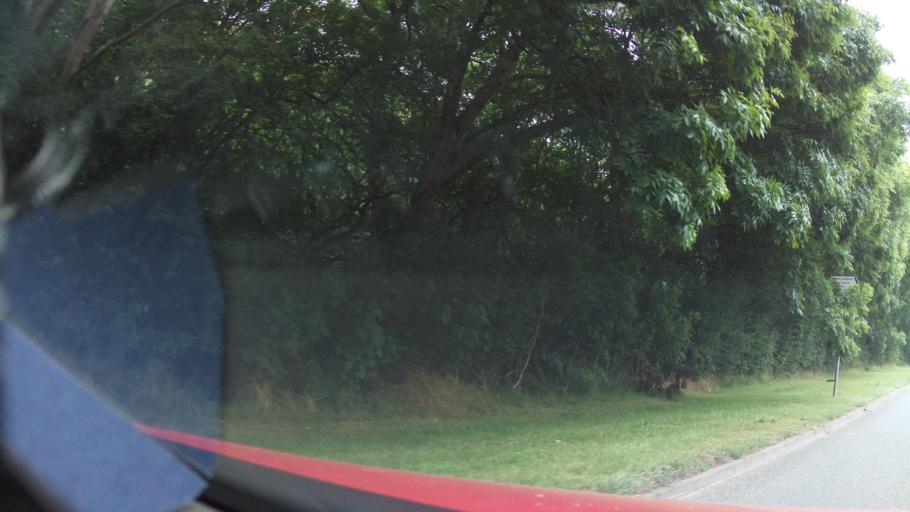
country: GB
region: England
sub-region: Northamptonshire
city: Corby
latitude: 52.5093
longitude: -0.7144
